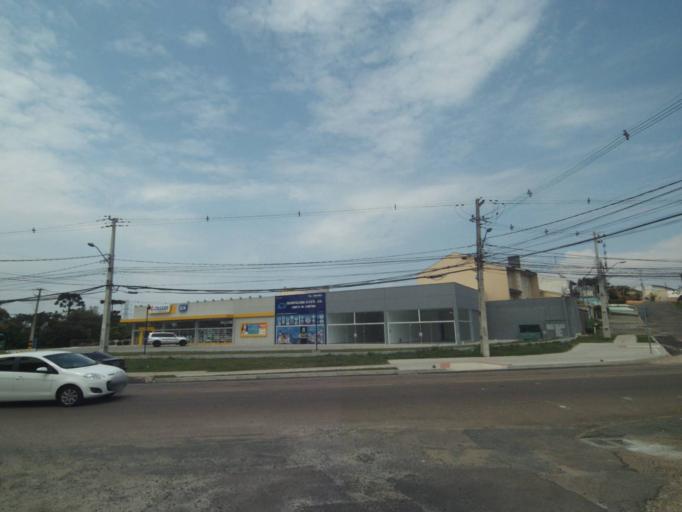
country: BR
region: Parana
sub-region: Curitiba
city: Curitiba
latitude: -25.4749
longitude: -49.3190
